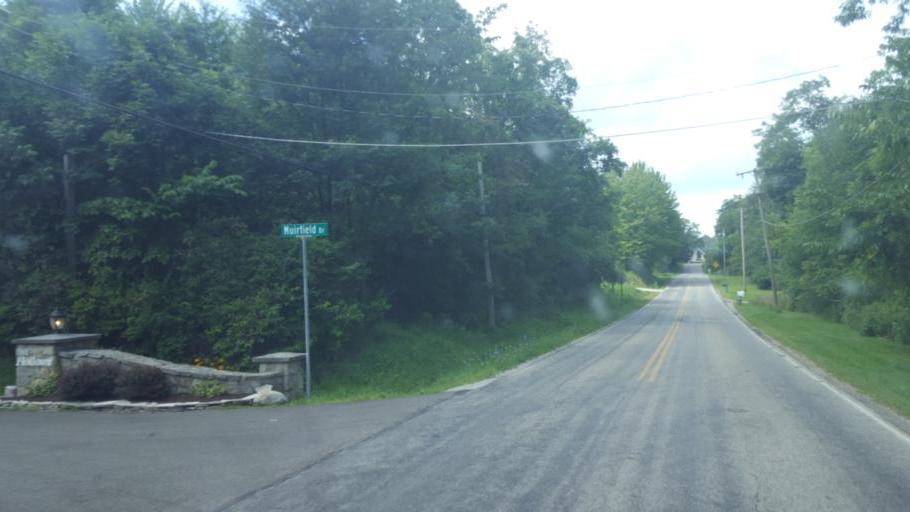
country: US
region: Ohio
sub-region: Richland County
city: Ontario
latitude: 40.7510
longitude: -82.6394
